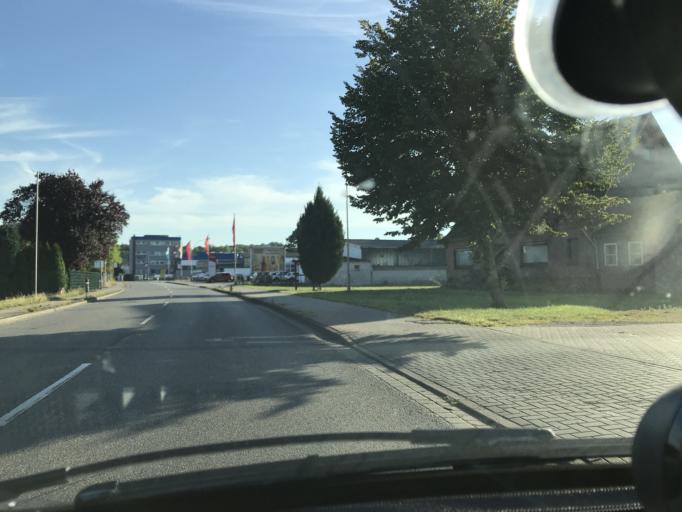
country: DE
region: Lower Saxony
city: Buxtehude
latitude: 53.4655
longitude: 9.7196
